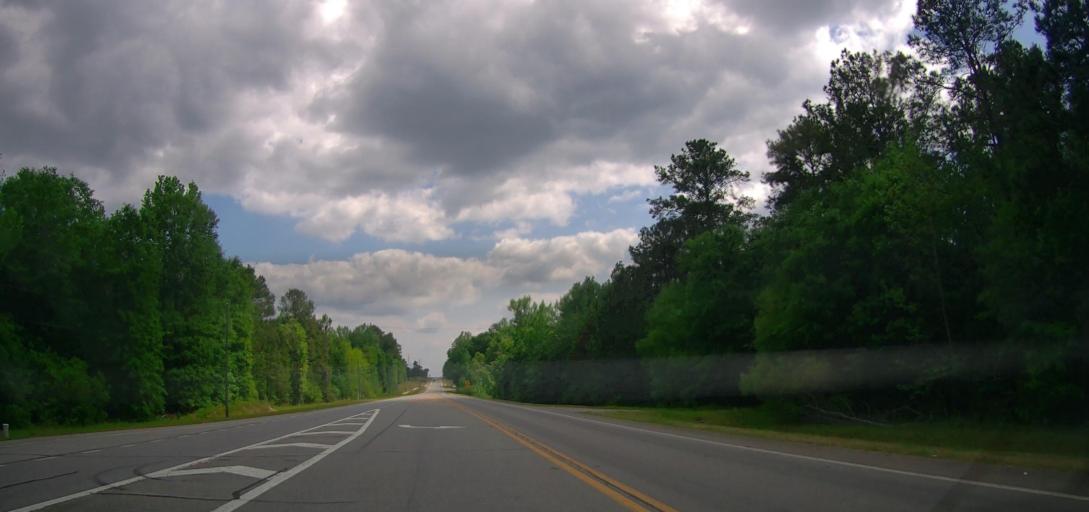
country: US
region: Georgia
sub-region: Laurens County
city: East Dublin
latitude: 32.5164
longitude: -82.8433
